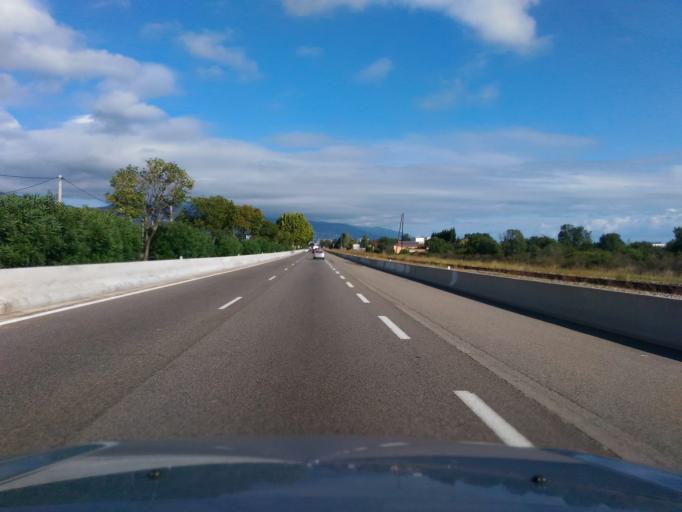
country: FR
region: Corsica
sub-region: Departement de la Haute-Corse
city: Biguglia
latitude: 42.6020
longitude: 9.4385
